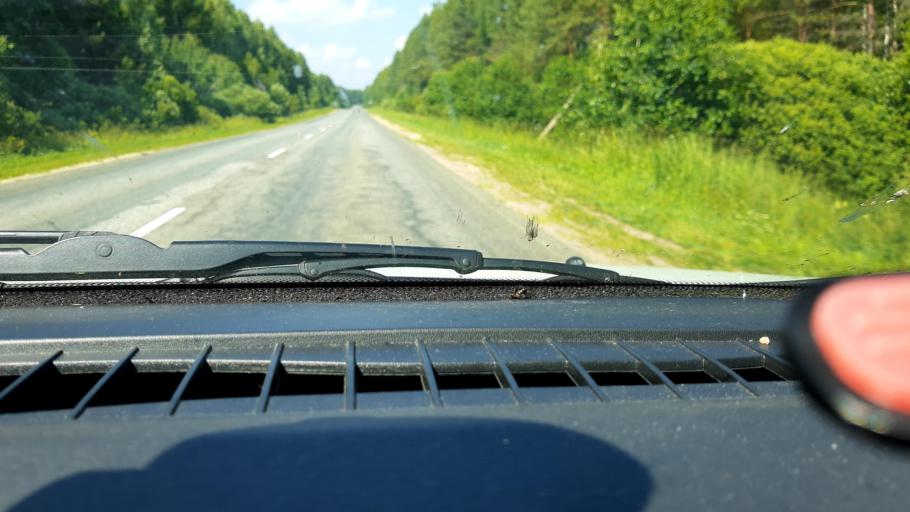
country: RU
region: Nizjnij Novgorod
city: Tonkino
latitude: 57.2884
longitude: 46.4620
